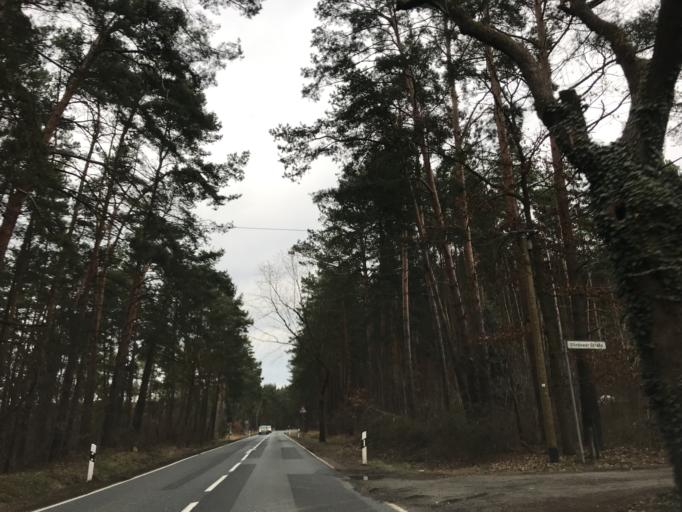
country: DE
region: Brandenburg
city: Fichtenwalde
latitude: 52.2972
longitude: 12.8613
